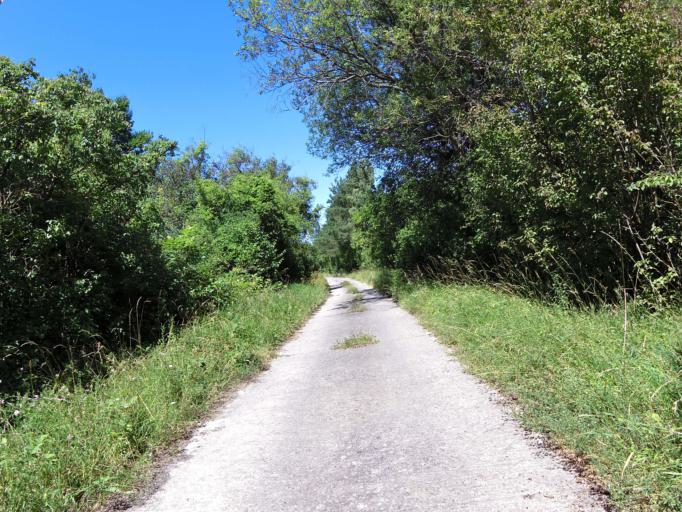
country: DE
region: Bavaria
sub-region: Regierungsbezirk Unterfranken
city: Gerbrunn
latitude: 49.7616
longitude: 9.9972
